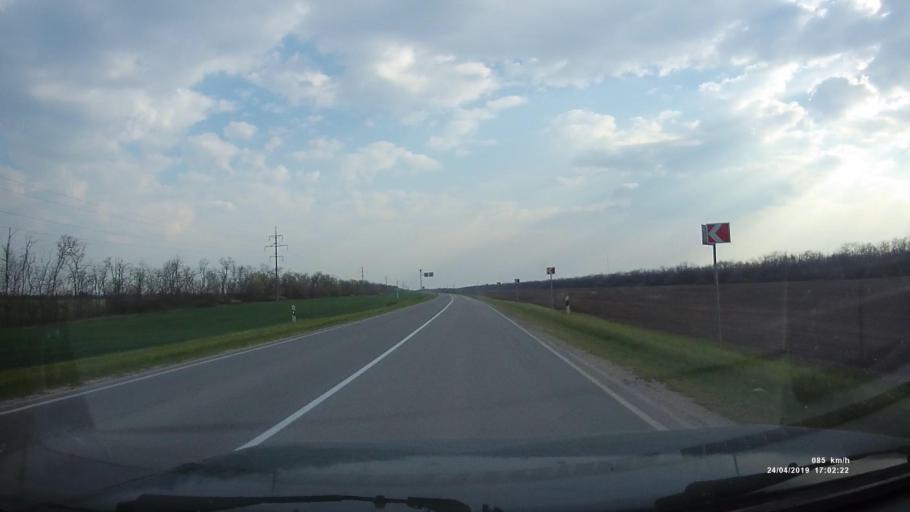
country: RU
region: Rostov
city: Sal'sk
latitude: 46.5814
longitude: 41.6159
